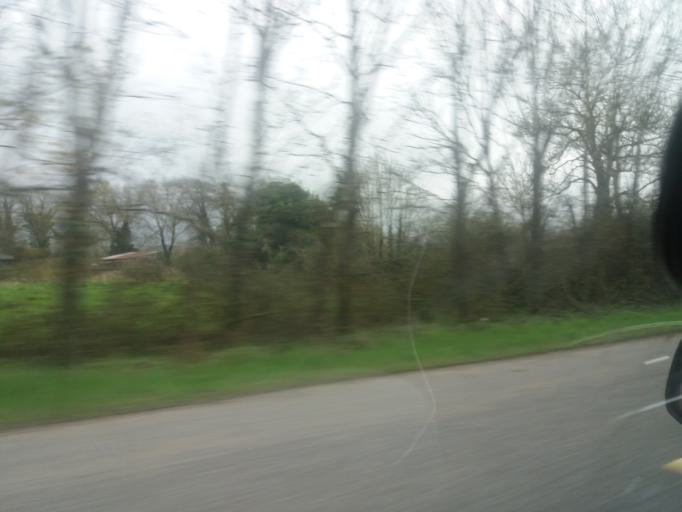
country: IE
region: Munster
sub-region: County Limerick
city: Rathkeale
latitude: 52.4981
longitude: -8.9947
